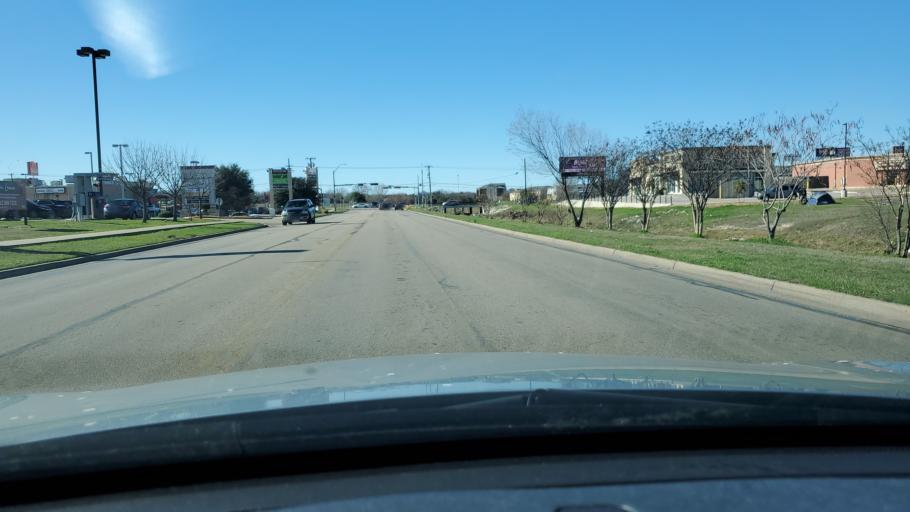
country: US
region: Texas
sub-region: Bell County
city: Killeen
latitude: 31.0921
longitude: -97.7313
